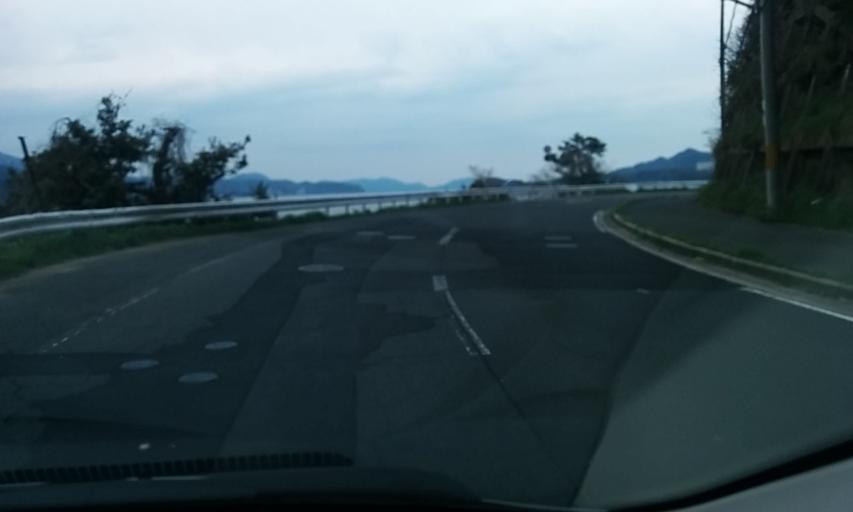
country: JP
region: Kyoto
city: Miyazu
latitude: 35.5618
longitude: 135.2071
